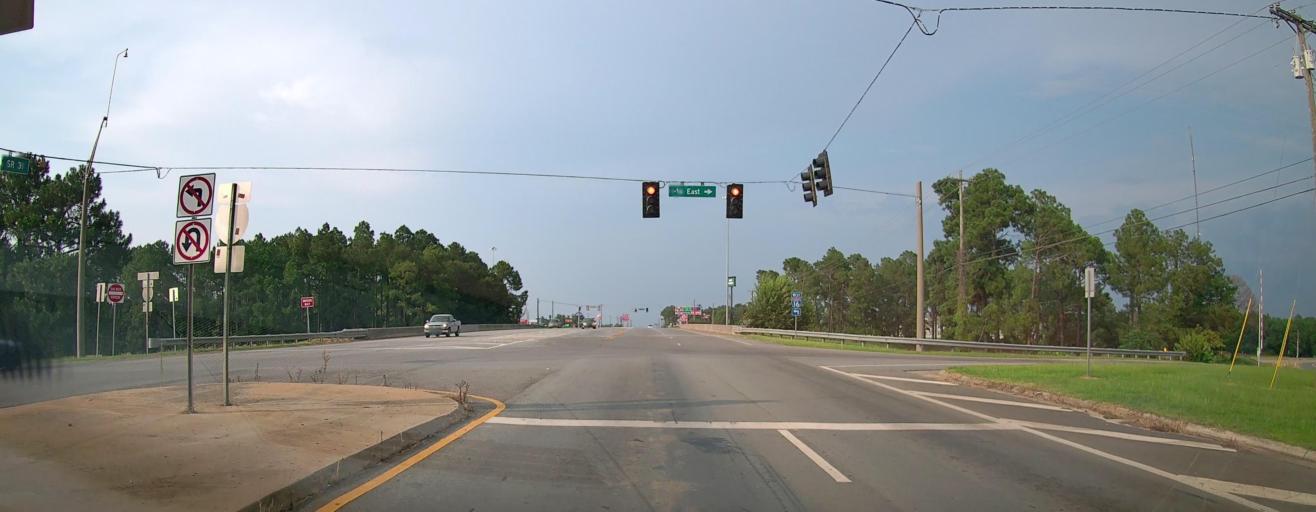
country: US
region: Georgia
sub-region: Laurens County
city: Dublin
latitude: 32.4868
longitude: -82.9358
